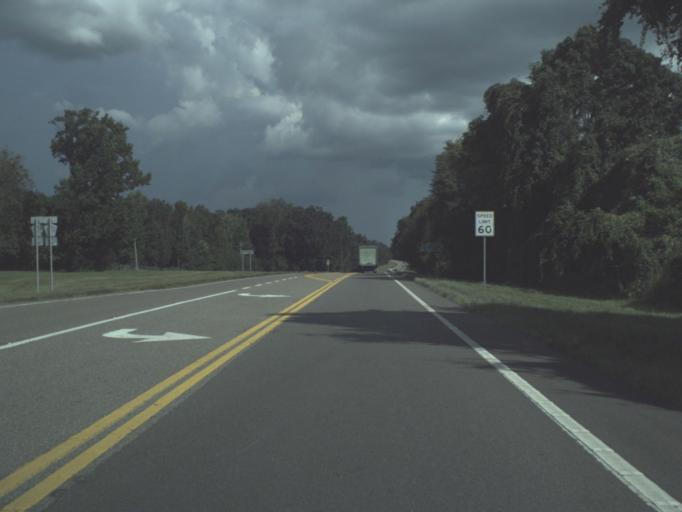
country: US
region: Florida
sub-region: Hernando County
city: North Brooksville
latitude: 28.6506
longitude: -82.4464
